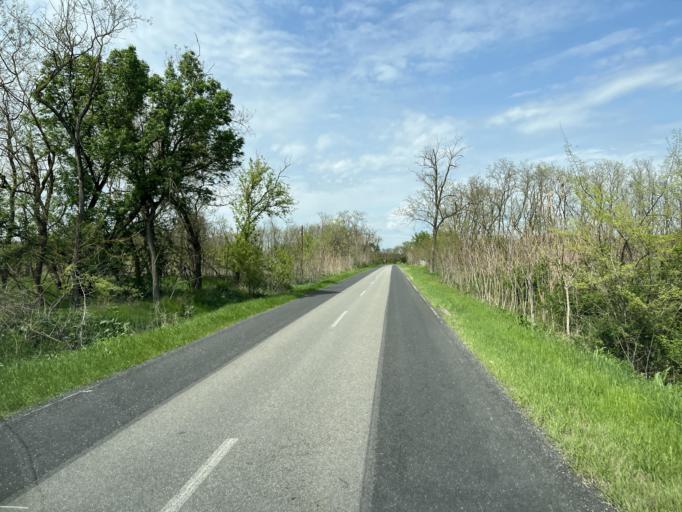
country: HU
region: Pest
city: Albertirsa
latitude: 47.1714
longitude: 19.6139
